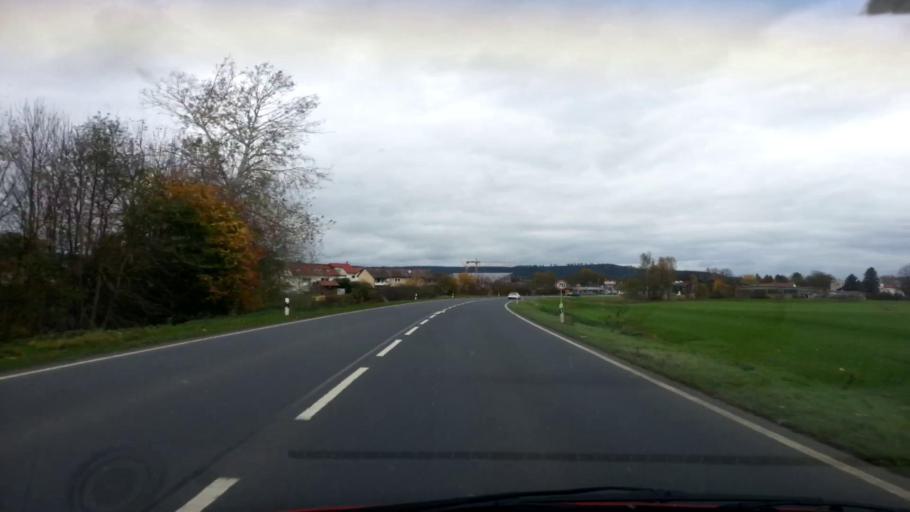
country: DE
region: Bavaria
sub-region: Upper Franconia
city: Kueps Oberfranken
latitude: 50.1886
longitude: 11.2643
